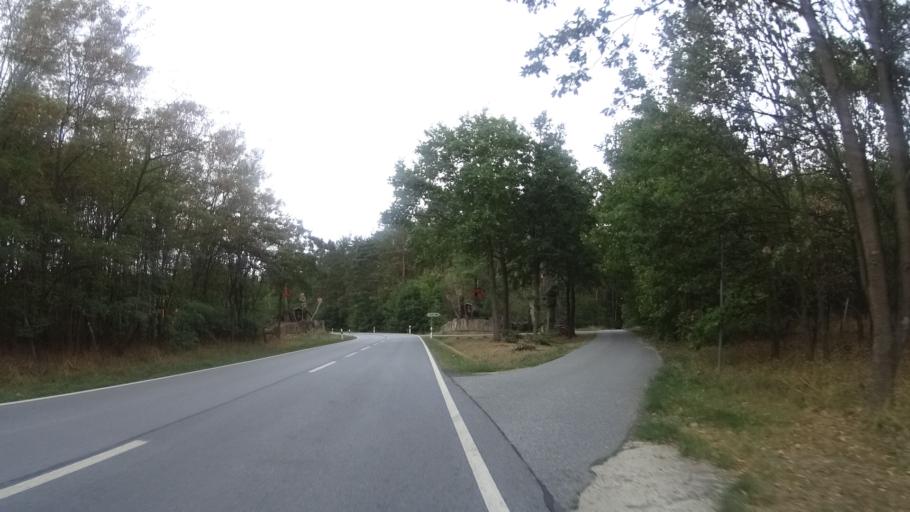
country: PL
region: Lower Silesian Voivodeship
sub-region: Powiat zgorzelecki
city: Piensk
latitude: 51.2913
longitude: 15.0231
